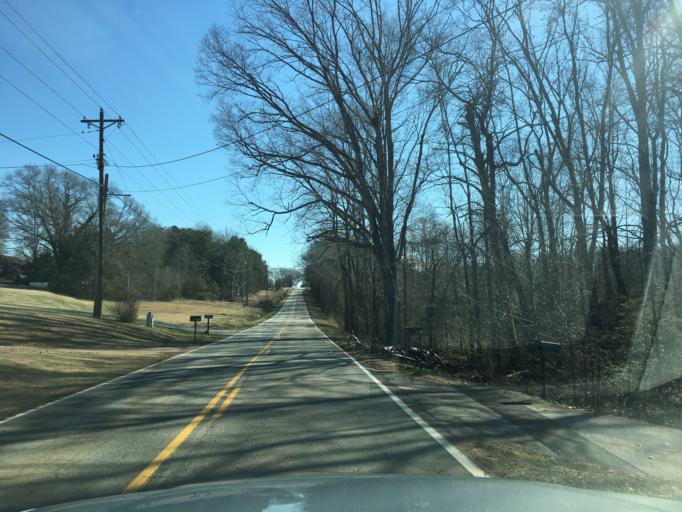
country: US
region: South Carolina
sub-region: Pickens County
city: Liberty
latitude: 34.8003
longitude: -82.7432
